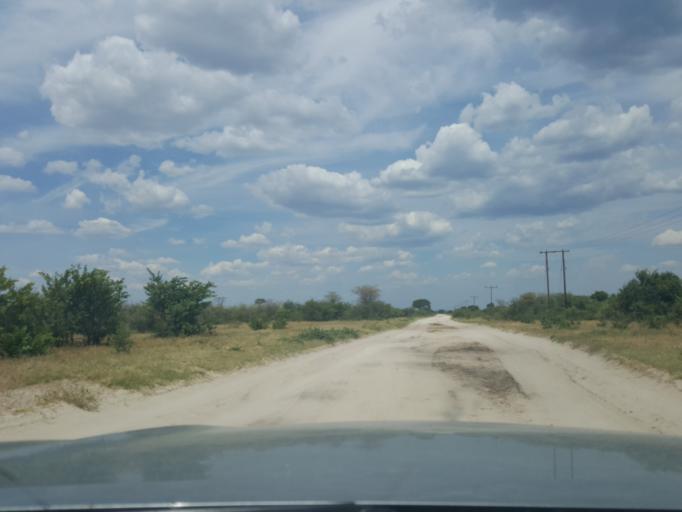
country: BW
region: North West
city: Shakawe
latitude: -18.5027
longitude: 22.1351
